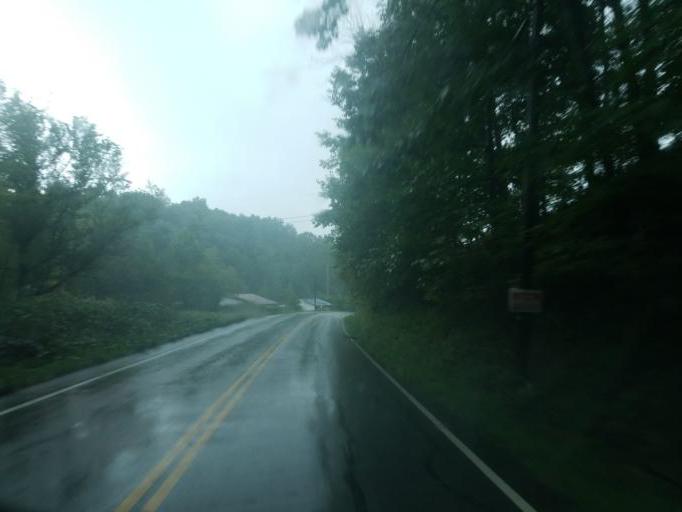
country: US
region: Kentucky
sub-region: Carter County
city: Olive Hill
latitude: 38.2733
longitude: -83.3144
